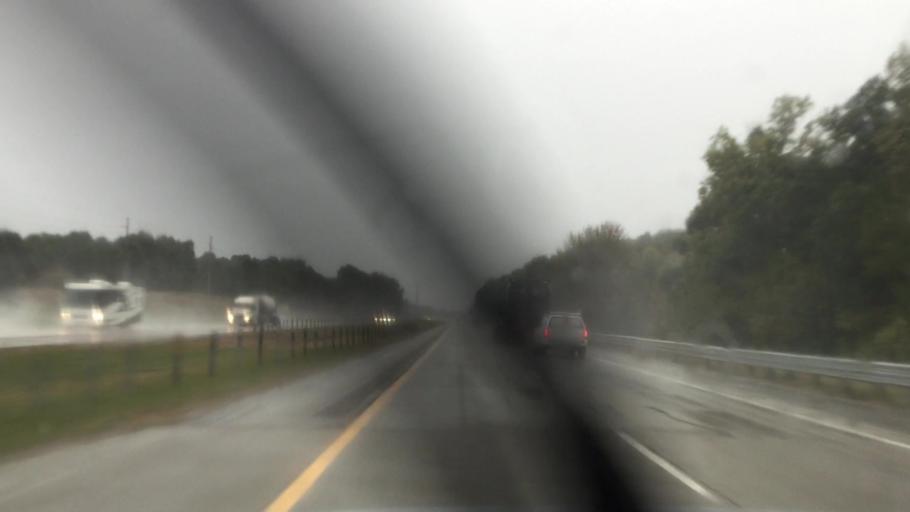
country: US
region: Michigan
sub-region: Van Buren County
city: Paw Paw
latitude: 42.2140
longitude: -85.8643
